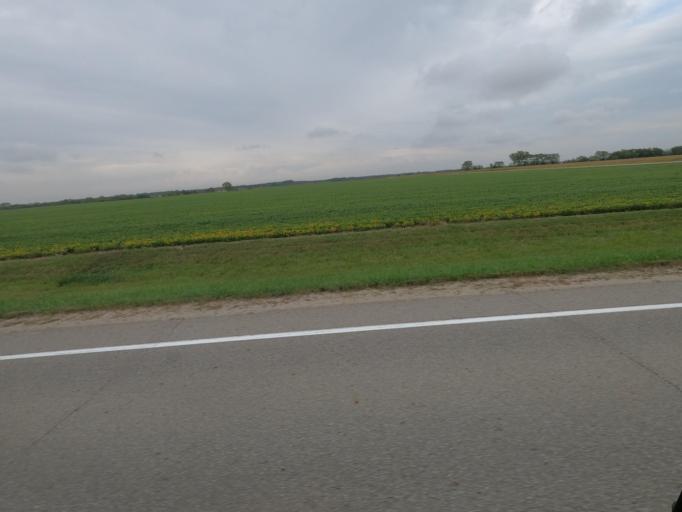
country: US
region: Iowa
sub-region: Van Buren County
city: Keosauqua
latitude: 40.8135
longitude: -91.8640
